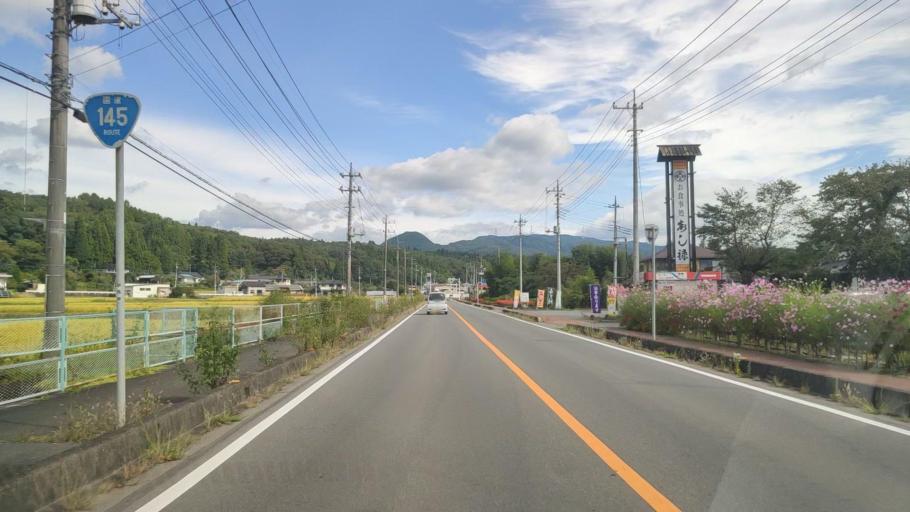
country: JP
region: Gunma
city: Nakanojomachi
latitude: 36.5970
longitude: 138.8630
